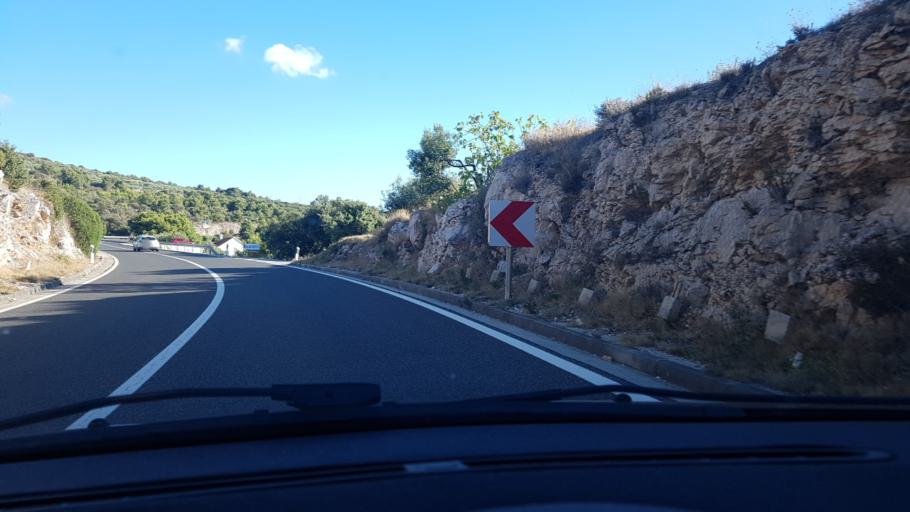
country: HR
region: Sibensko-Kniniska
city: Primosten
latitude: 43.6103
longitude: 15.9260
